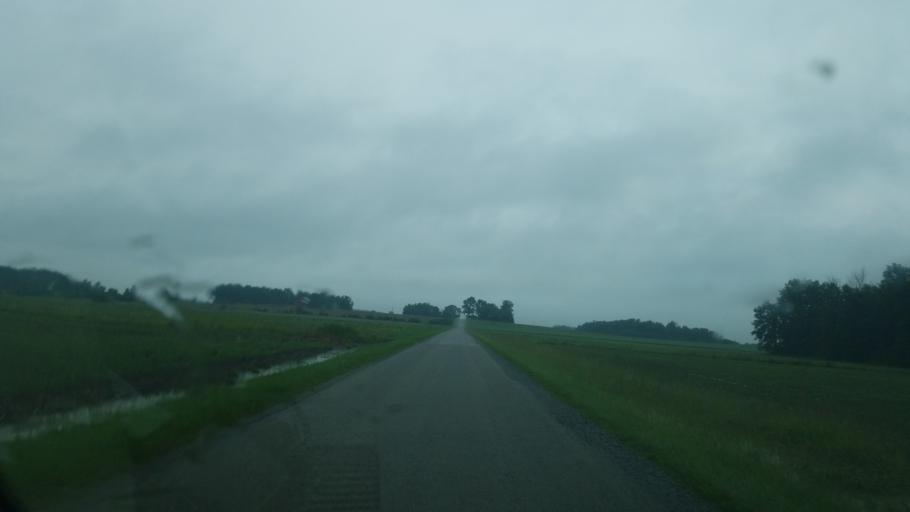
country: US
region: Ohio
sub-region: Huron County
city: Willard
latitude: 40.9377
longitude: -82.7974
